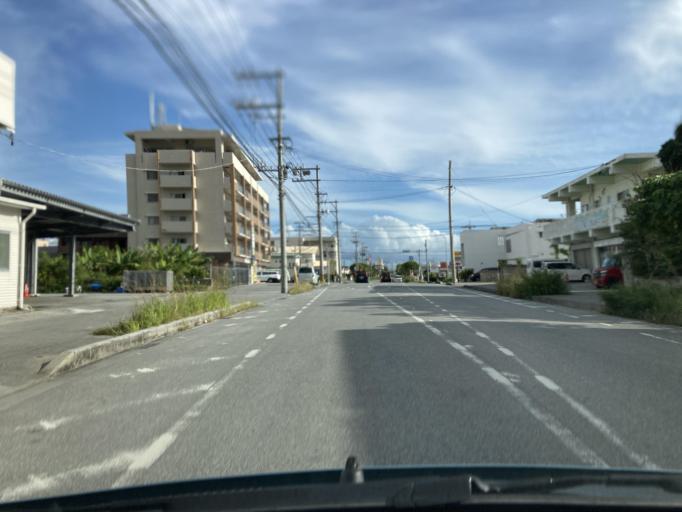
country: JP
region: Okinawa
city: Okinawa
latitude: 26.3359
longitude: 127.8363
